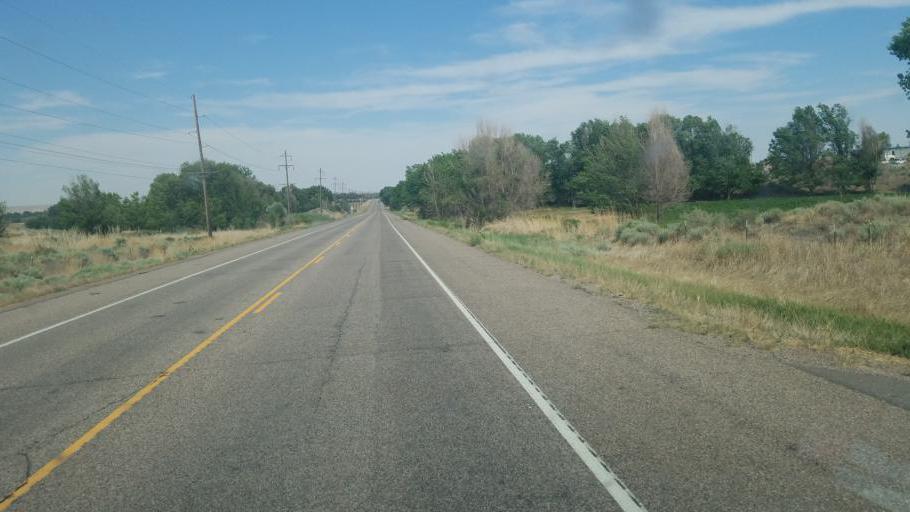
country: US
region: Colorado
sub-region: Otero County
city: Fowler
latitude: 38.2290
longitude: -104.2821
